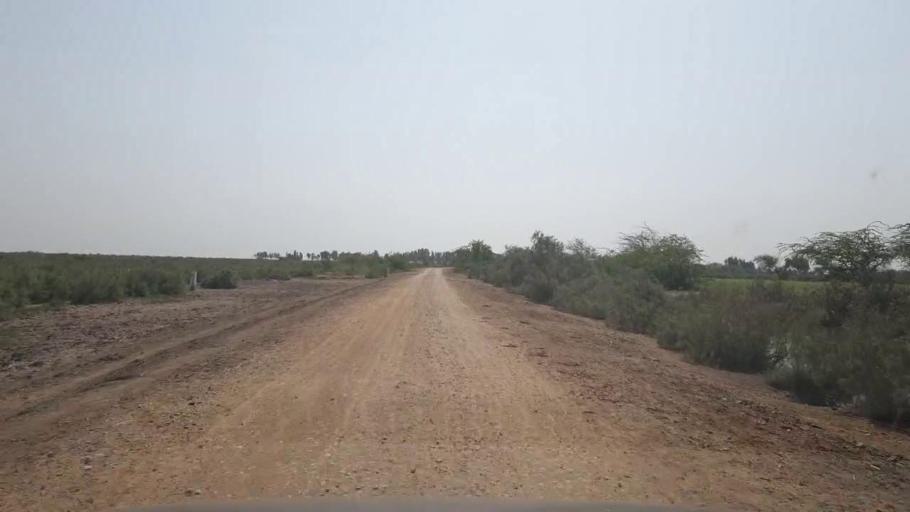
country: PK
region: Sindh
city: Jati
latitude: 24.3828
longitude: 68.6009
